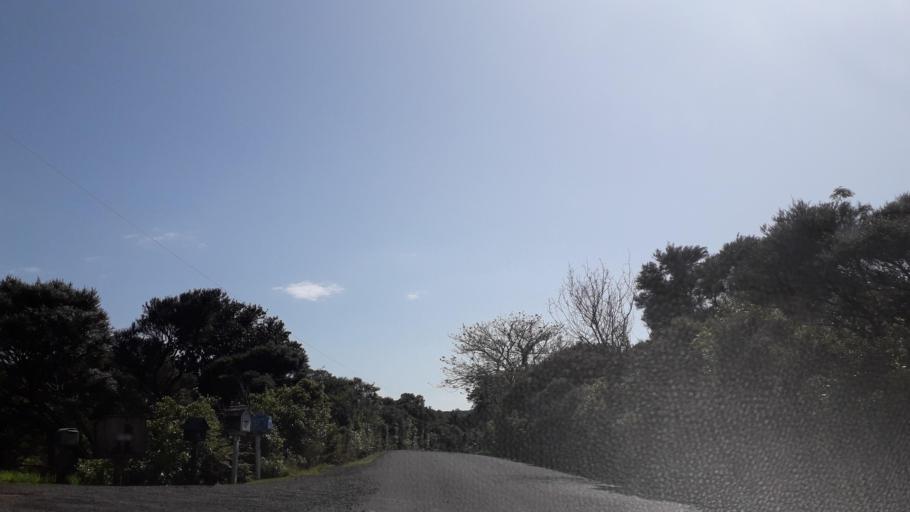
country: NZ
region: Northland
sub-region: Far North District
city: Paihia
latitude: -35.2304
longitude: 174.2614
